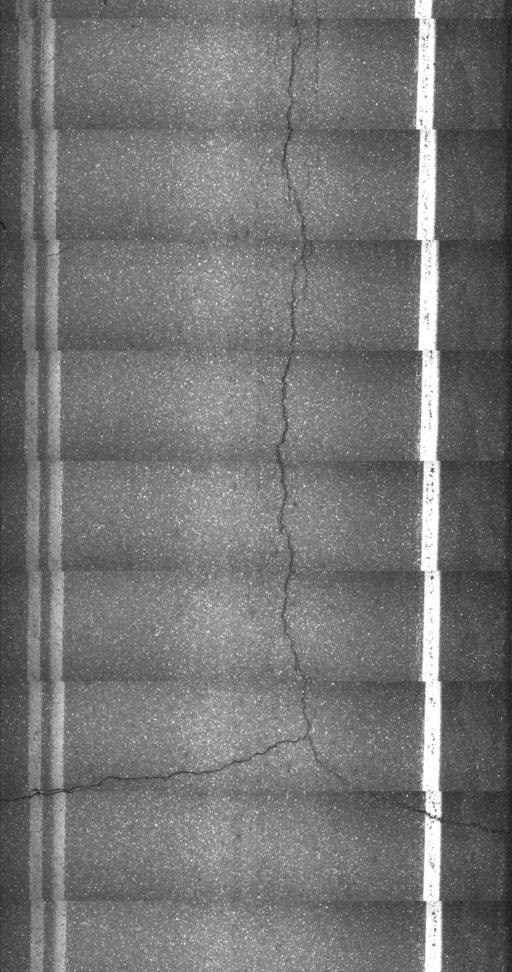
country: US
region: Vermont
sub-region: Caledonia County
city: Lyndonville
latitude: 44.6408
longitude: -72.1535
